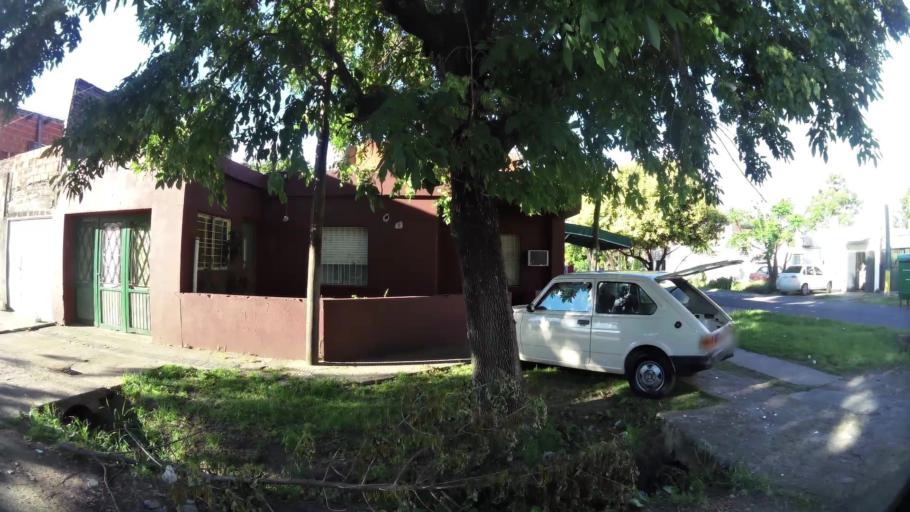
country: AR
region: Santa Fe
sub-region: Departamento de Rosario
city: Rosario
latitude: -32.9876
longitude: -60.6829
